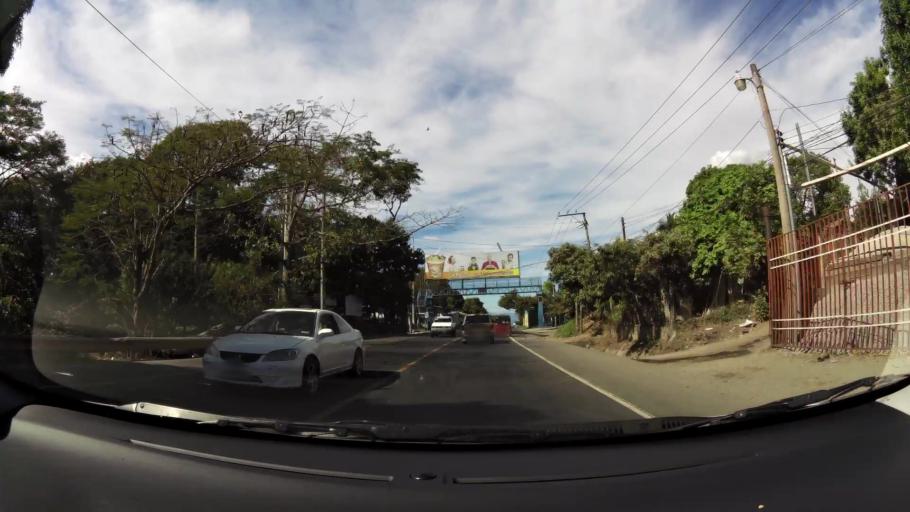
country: SV
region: San Salvador
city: Guazapa
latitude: 13.8739
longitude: -89.1727
